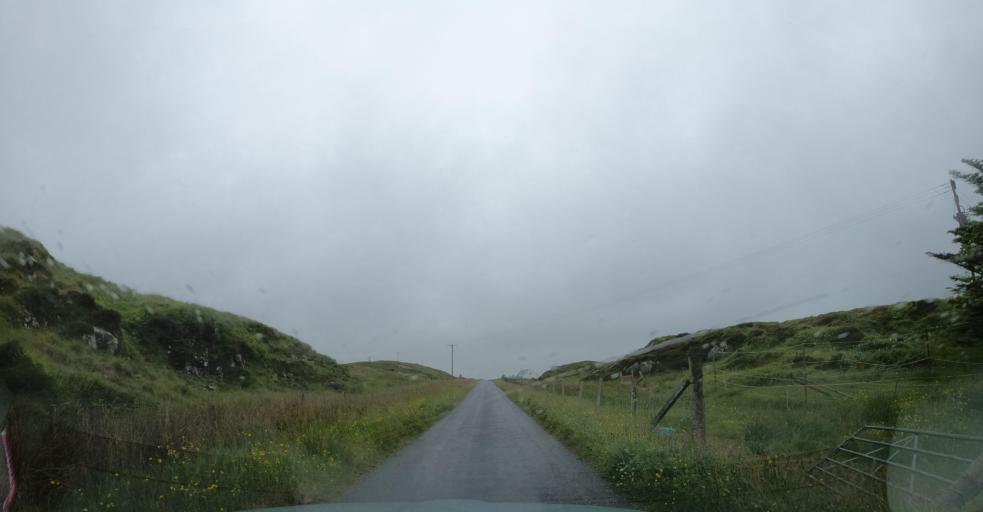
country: GB
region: Scotland
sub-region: Eilean Siar
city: Benbecula
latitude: 57.4814
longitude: -7.2062
